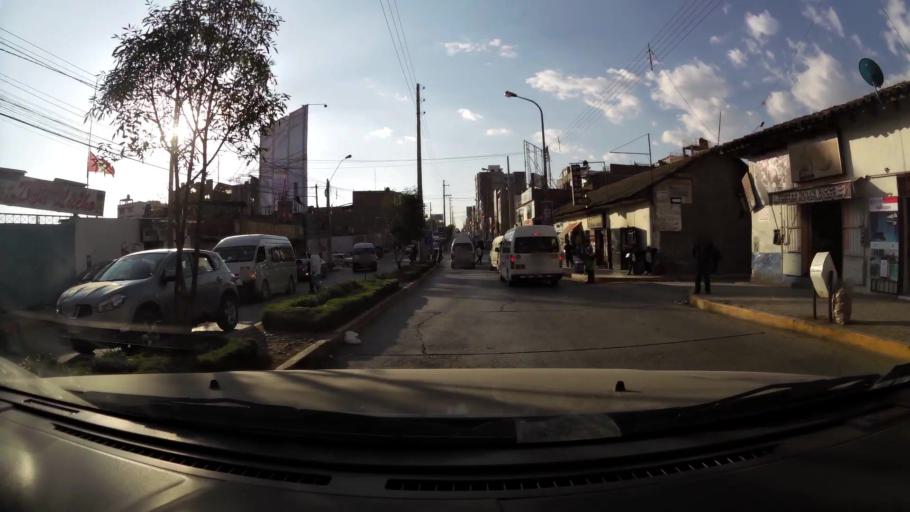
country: PE
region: Junin
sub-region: Provincia de Huancayo
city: El Tambo
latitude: -12.0500
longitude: -75.2218
